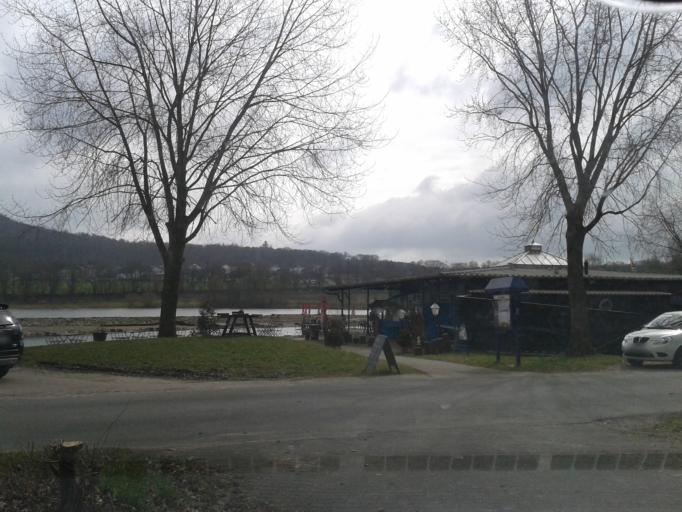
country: DE
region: North Rhine-Westphalia
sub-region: Regierungsbezirk Detmold
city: Schieder-Schwalenberg
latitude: 51.9222
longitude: 9.1557
